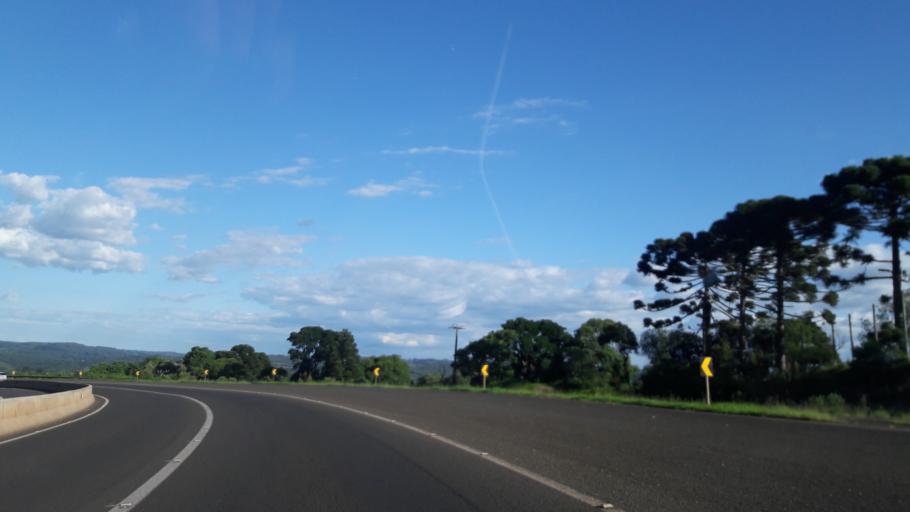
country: BR
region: Parana
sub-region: Guarapuava
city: Guarapuava
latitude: -25.3484
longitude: -51.3909
